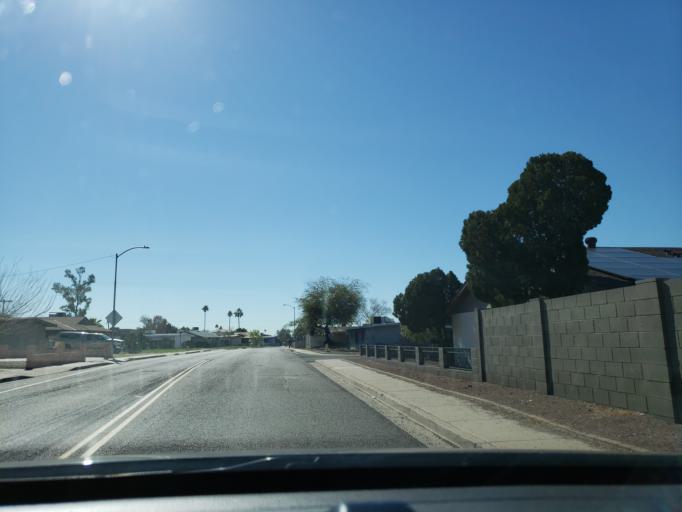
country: US
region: Arizona
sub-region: Maricopa County
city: Glendale
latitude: 33.6200
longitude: -112.1249
